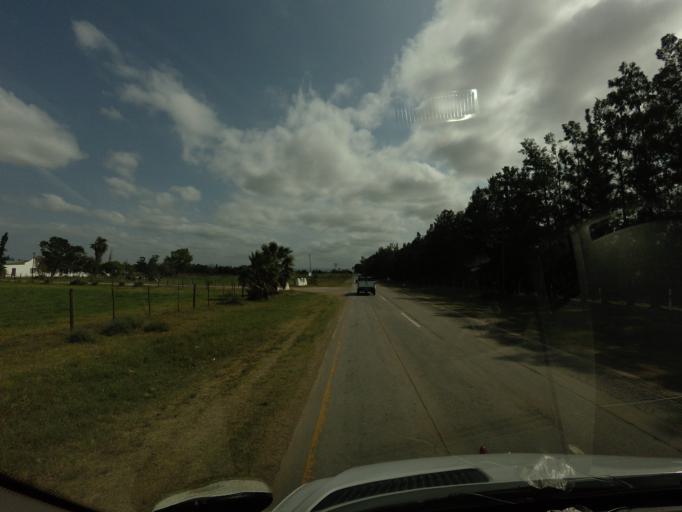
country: ZA
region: Eastern Cape
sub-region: Cacadu District Municipality
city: Kirkwood
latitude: -33.5327
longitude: 25.6911
